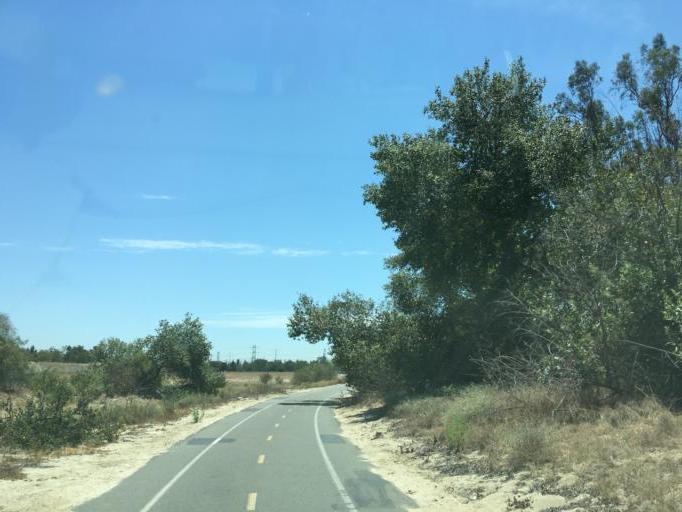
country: US
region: California
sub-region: Los Angeles County
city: South San Gabriel
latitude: 34.0478
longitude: -118.0712
